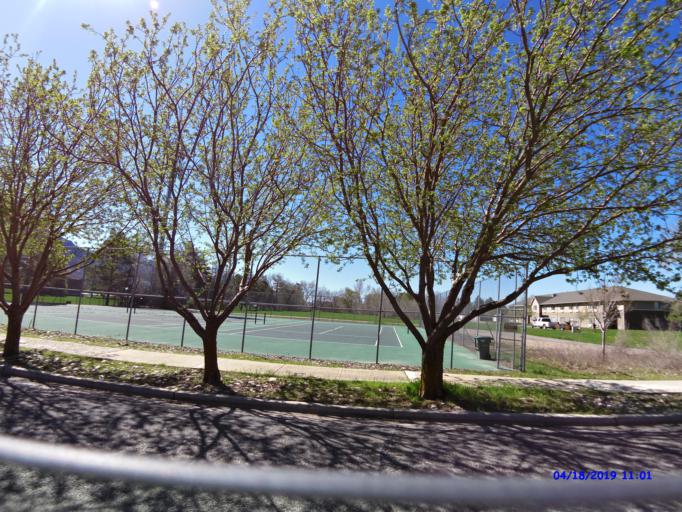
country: US
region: Utah
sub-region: Weber County
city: Harrisville
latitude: 41.2831
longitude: -111.9674
